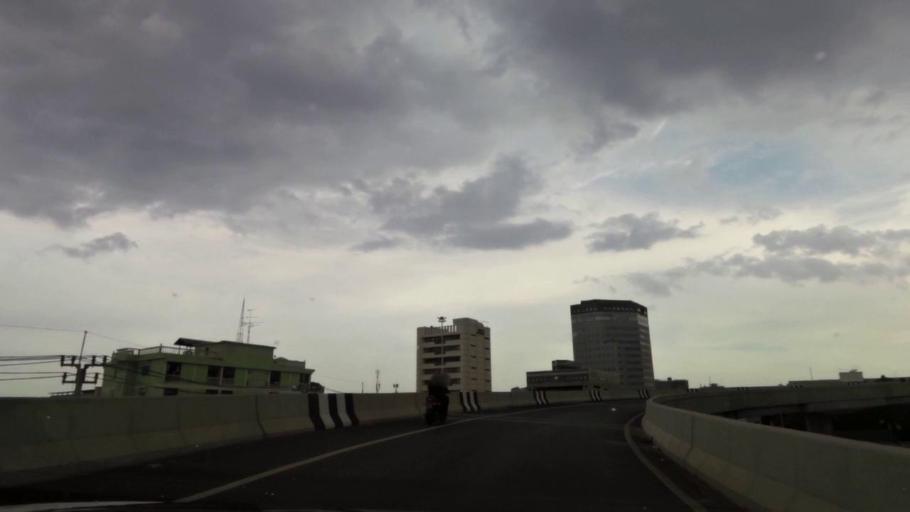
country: TH
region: Bangkok
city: Bang Kapi
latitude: 13.7521
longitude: 100.6473
